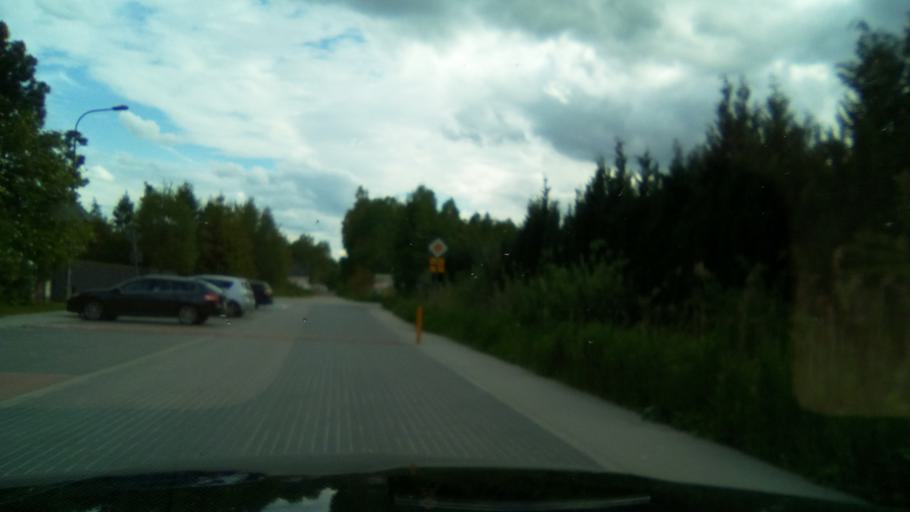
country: PL
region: Pomeranian Voivodeship
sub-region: Powiat pucki
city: Wierzchucino
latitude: 54.8267
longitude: 18.0763
